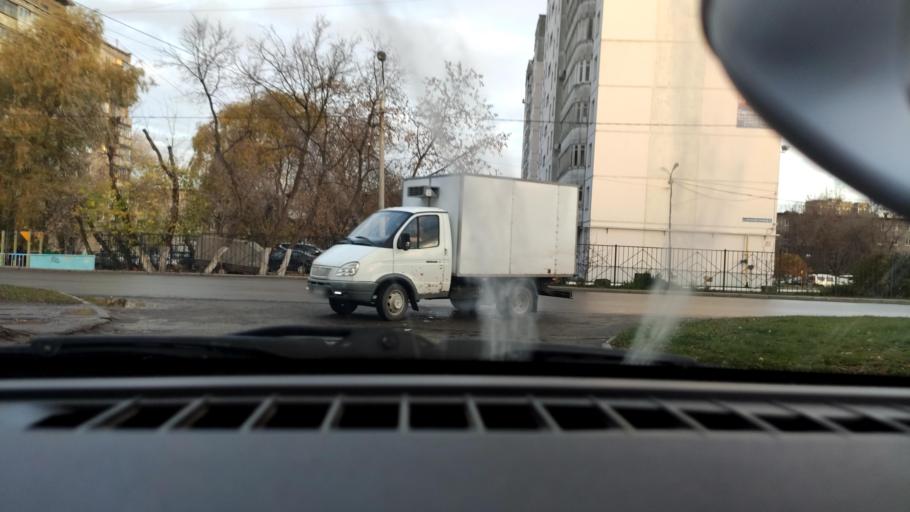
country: RU
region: Perm
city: Kondratovo
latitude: 57.9682
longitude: 56.1651
